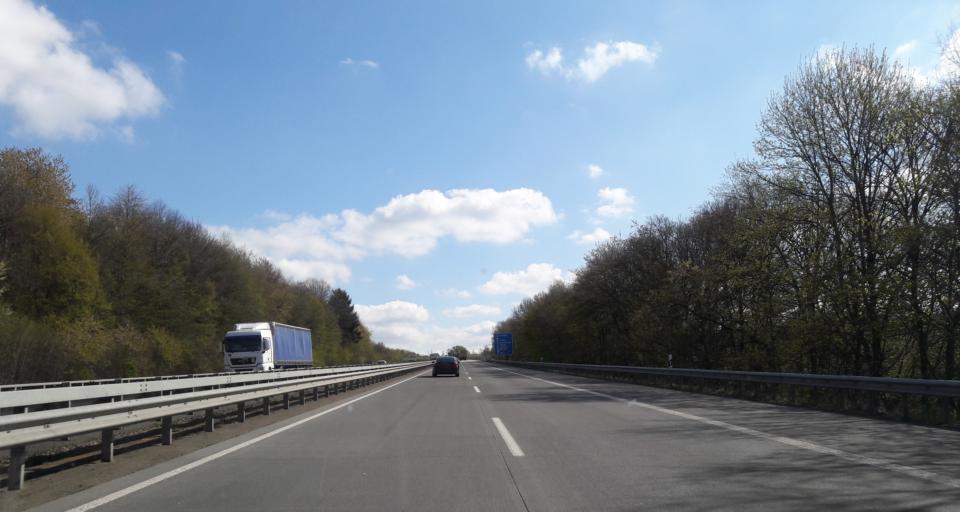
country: DE
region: Rheinland-Pfalz
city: Ulmen
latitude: 50.2028
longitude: 6.9637
